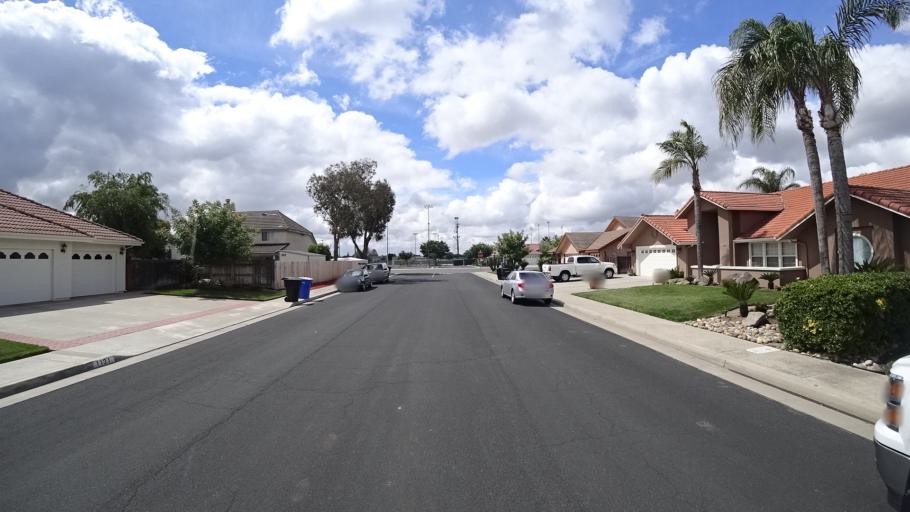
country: US
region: California
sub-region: Kings County
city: Hanford
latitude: 36.3366
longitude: -119.6669
